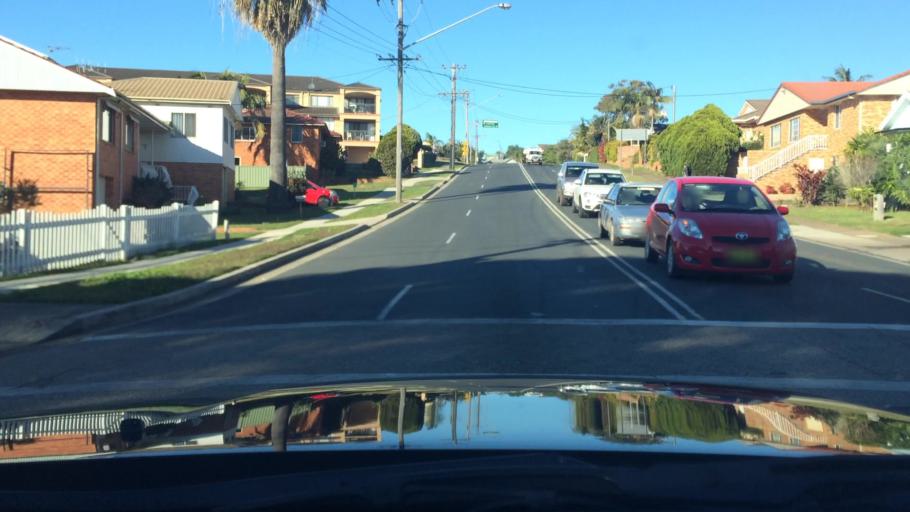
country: AU
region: New South Wales
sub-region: Port Macquarie-Hastings
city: Port Macquarie
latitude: -31.4314
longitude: 152.8996
